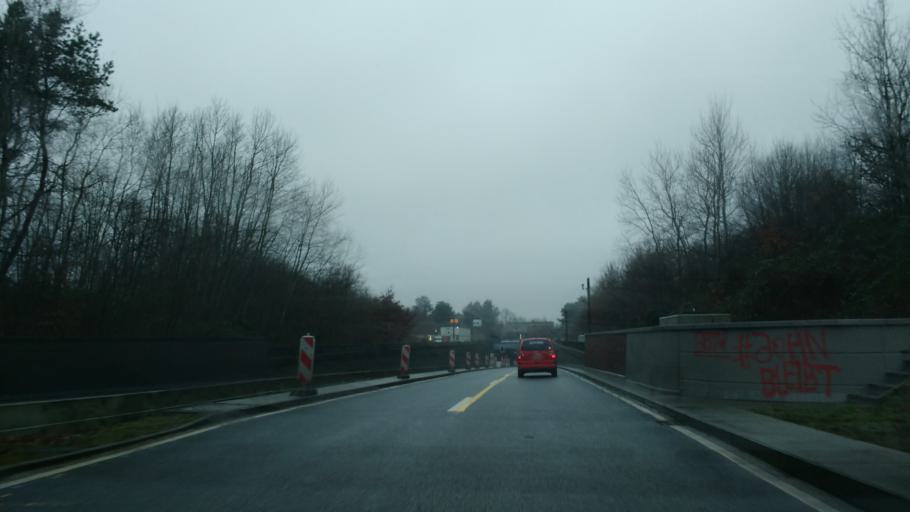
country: DE
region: Schleswig-Holstein
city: Westerronfeld
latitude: 54.2835
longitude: 9.6578
